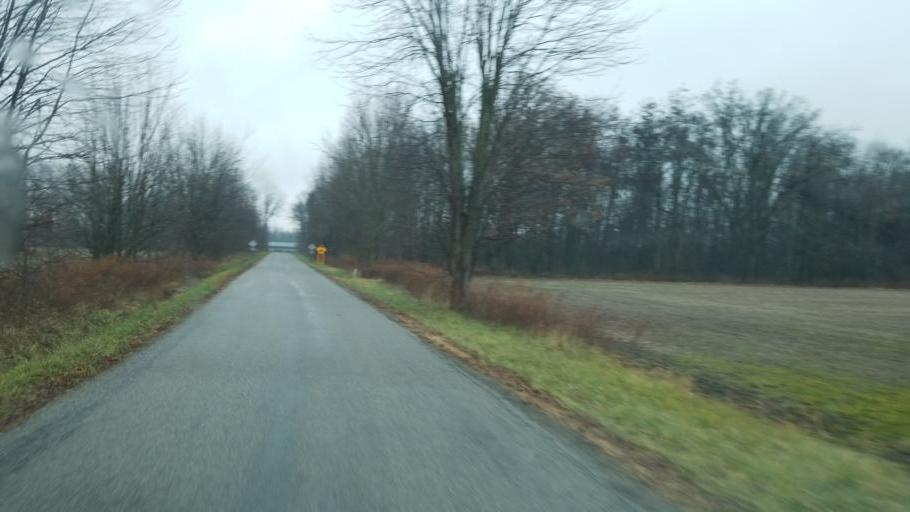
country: US
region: Ohio
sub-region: Licking County
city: Utica
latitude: 40.2539
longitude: -82.5547
